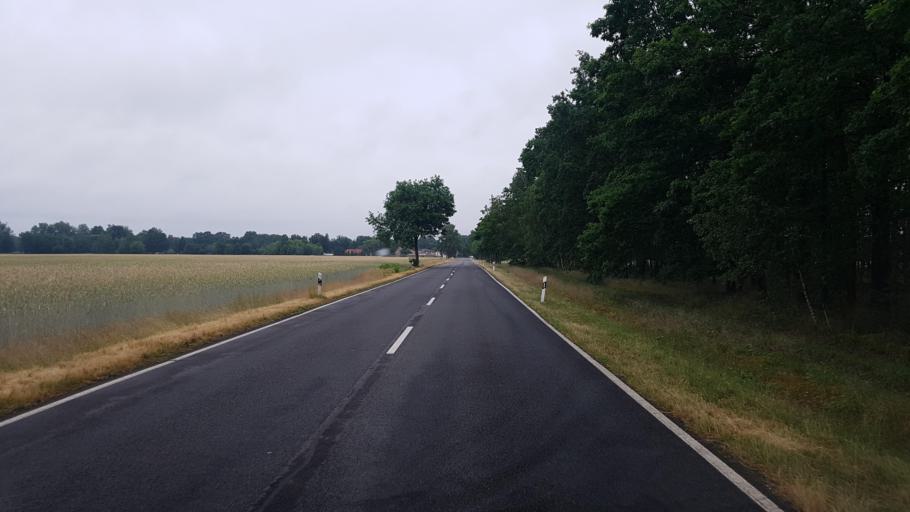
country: DE
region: Brandenburg
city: Kroppen
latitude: 51.3945
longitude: 13.8425
